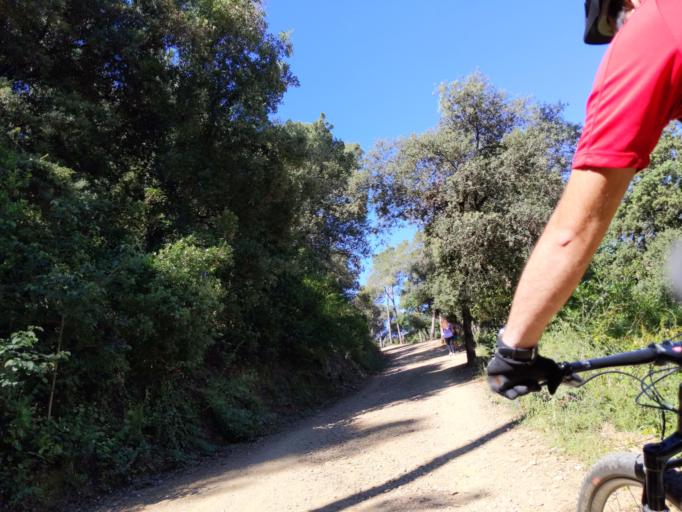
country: ES
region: Catalonia
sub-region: Provincia de Barcelona
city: Nou Barris
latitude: 41.4499
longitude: 2.1529
